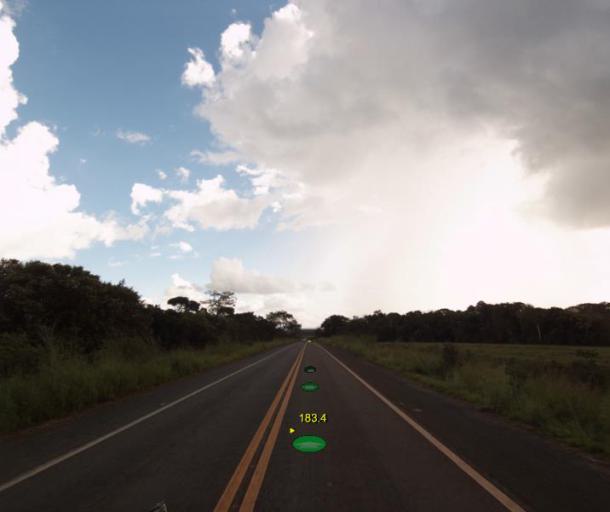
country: BR
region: Goias
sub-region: Itaberai
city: Itaberai
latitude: -15.9954
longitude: -49.7368
